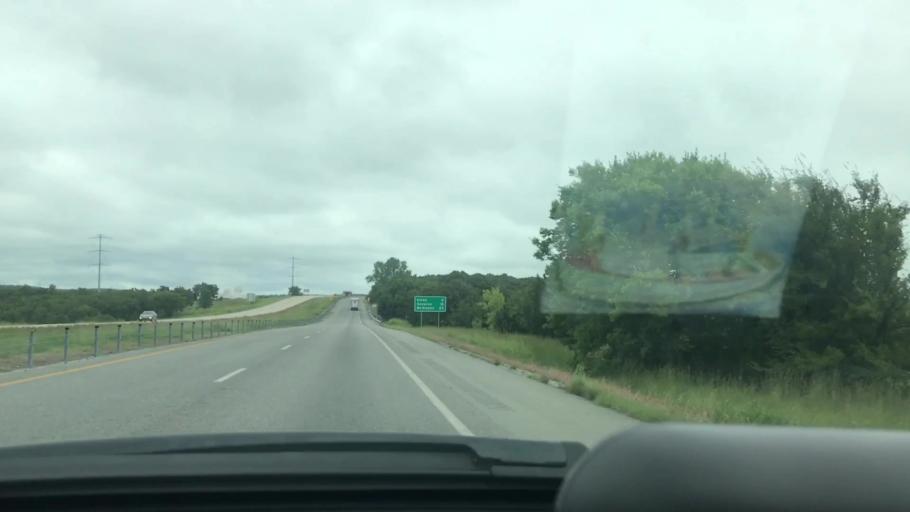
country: US
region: Oklahoma
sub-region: Pittsburg County
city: McAlester
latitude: 34.6713
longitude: -95.9361
